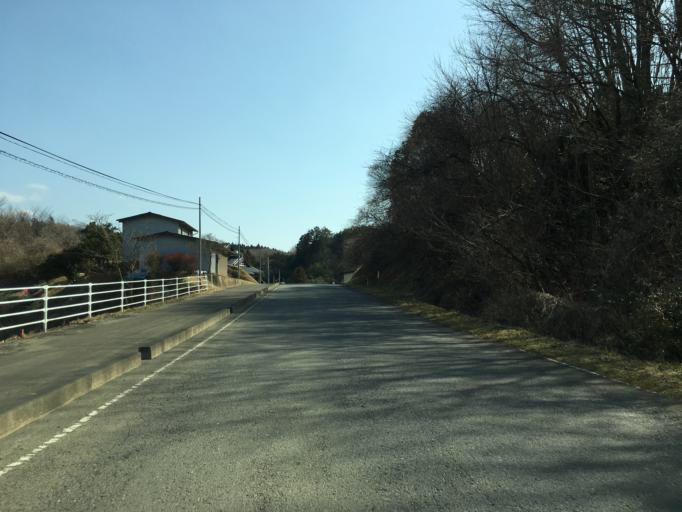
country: JP
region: Fukushima
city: Ishikawa
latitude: 37.1373
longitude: 140.4062
